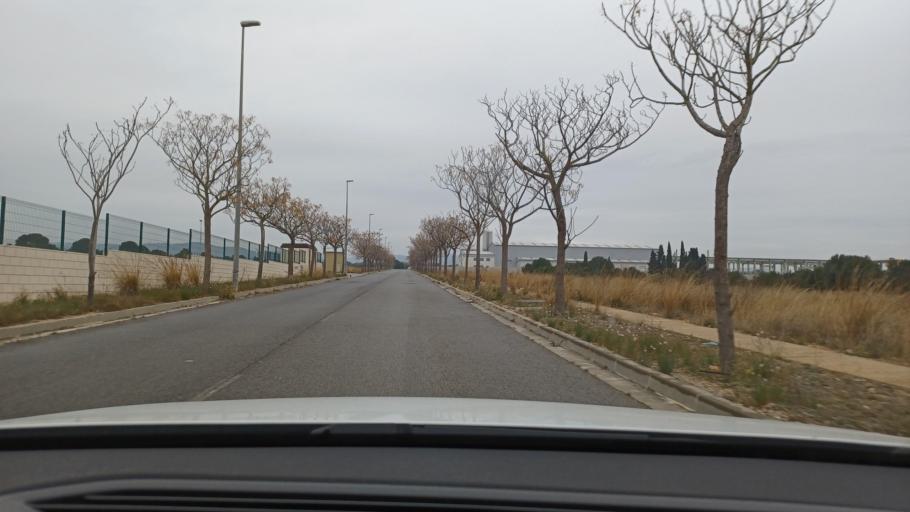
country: ES
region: Catalonia
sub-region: Provincia de Tarragona
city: Amposta
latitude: 40.7585
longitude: 0.6004
